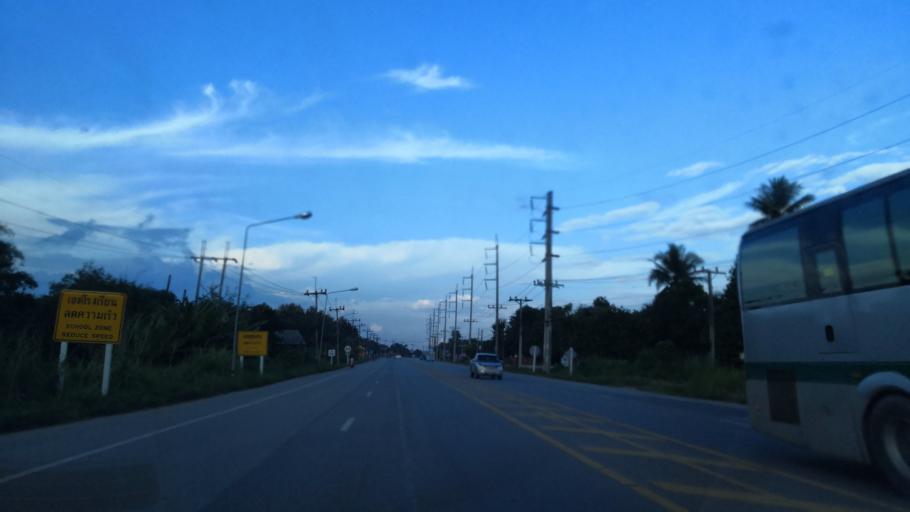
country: TH
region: Chiang Rai
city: Mae Suai
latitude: 19.6362
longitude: 99.5169
